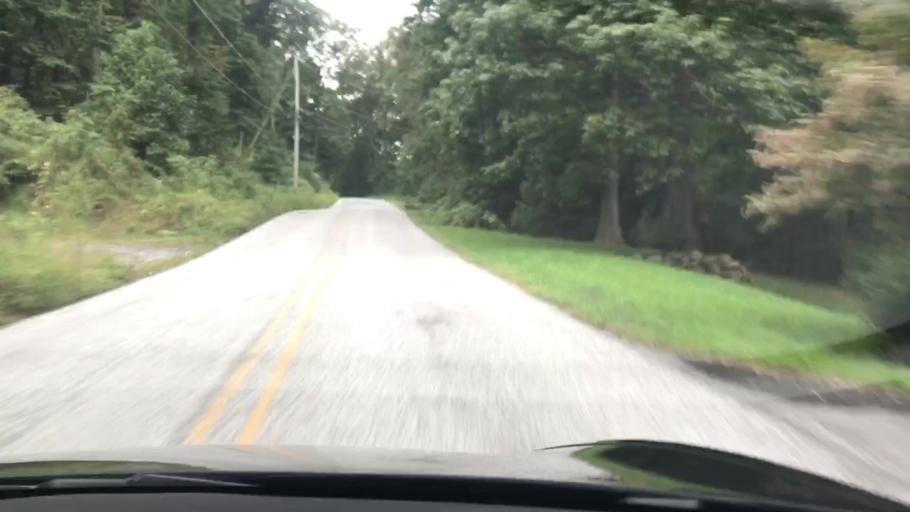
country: US
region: Pennsylvania
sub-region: York County
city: Dillsburg
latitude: 40.1120
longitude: -76.9659
